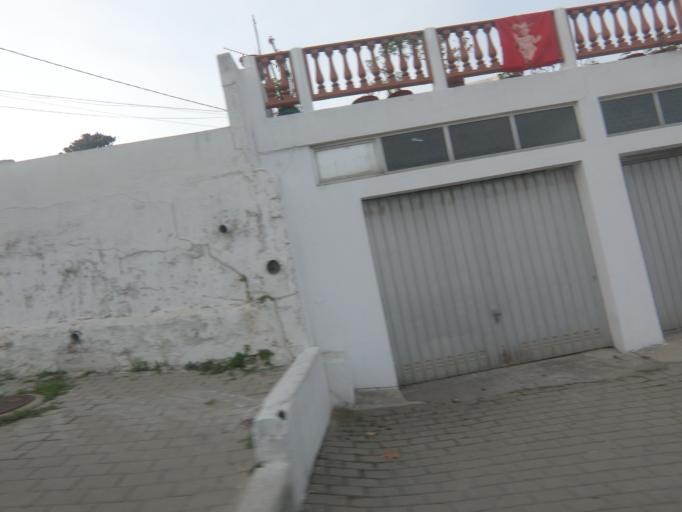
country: PT
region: Setubal
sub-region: Setubal
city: Setubal
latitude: 38.5283
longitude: -8.8667
